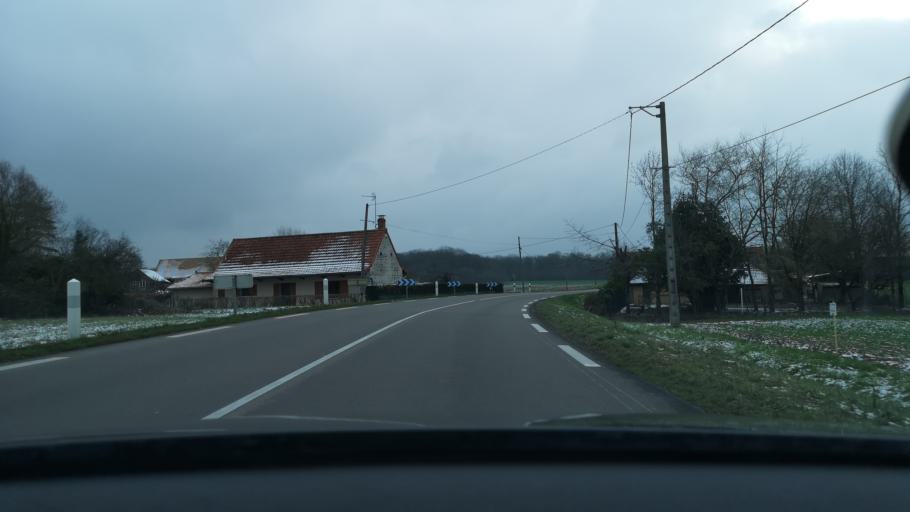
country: FR
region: Bourgogne
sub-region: Departement de Saone-et-Loire
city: Ouroux-sur-Saone
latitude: 46.7700
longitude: 4.9776
